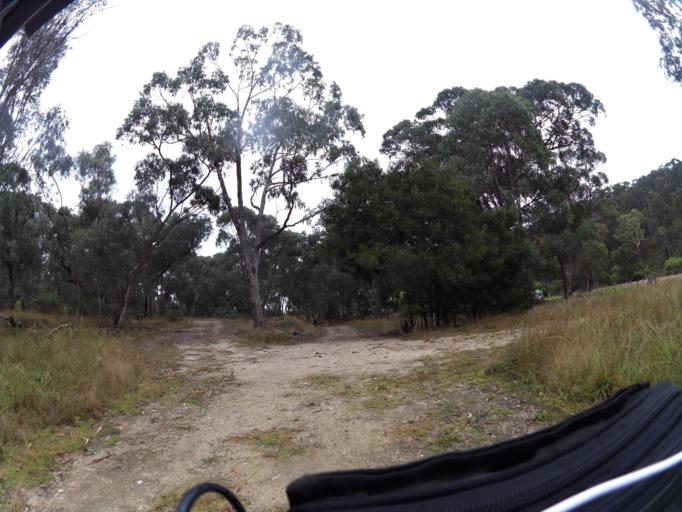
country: AU
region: New South Wales
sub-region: Greater Hume Shire
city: Holbrook
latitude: -36.1535
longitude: 147.4142
